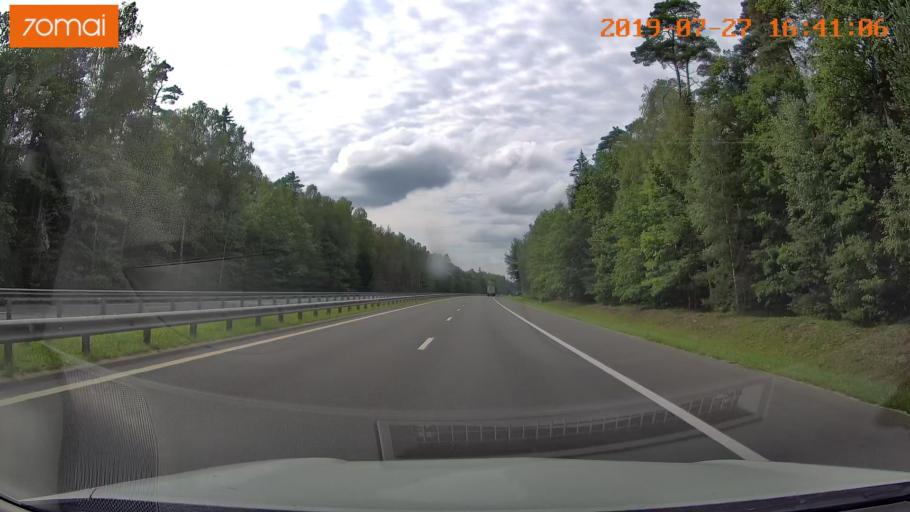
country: RU
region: Kaliningrad
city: Gvardeysk
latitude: 54.6527
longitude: 21.1554
